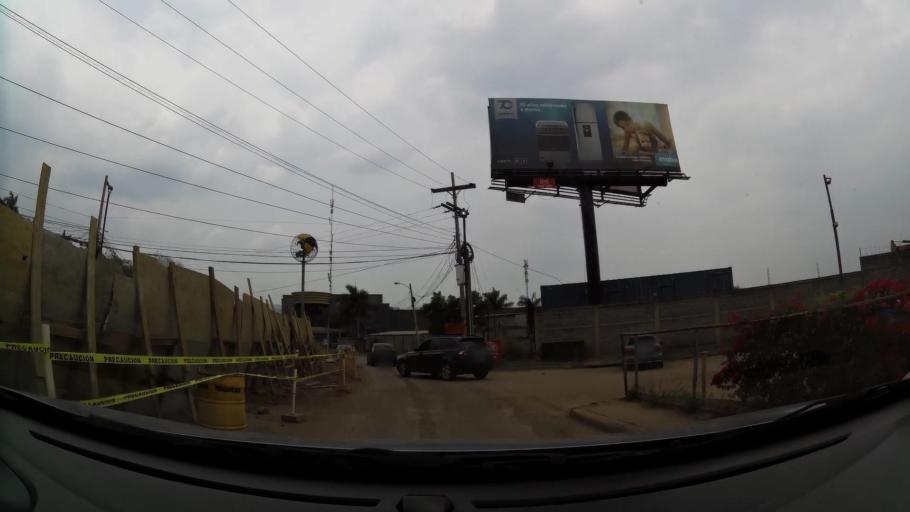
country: HN
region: Francisco Morazan
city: Tegucigalpa
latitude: 14.0832
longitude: -87.1695
